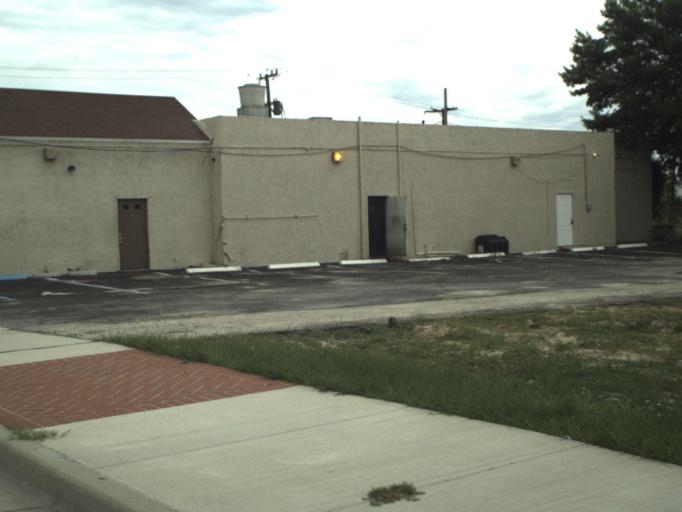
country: US
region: Florida
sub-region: Palm Beach County
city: Riviera Beach
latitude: 26.7758
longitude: -80.0549
